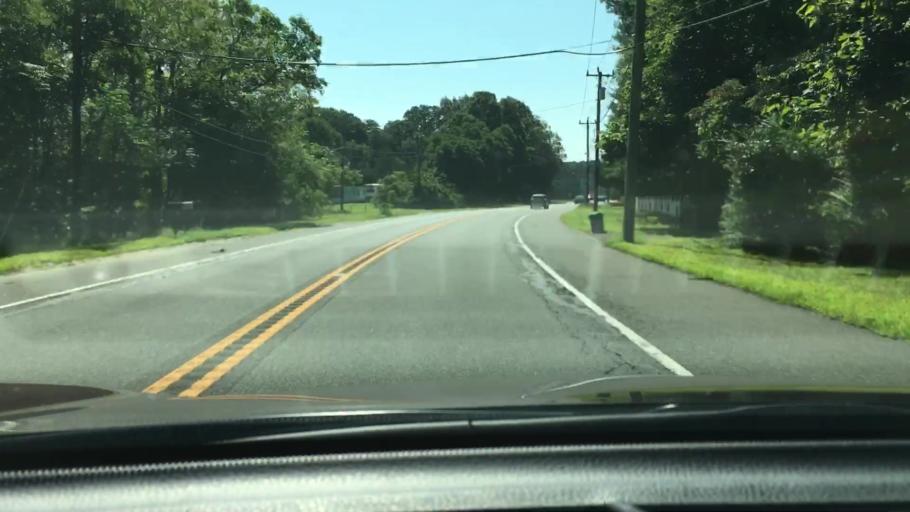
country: US
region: New Jersey
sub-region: Cumberland County
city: Laurel Lake
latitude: 39.3727
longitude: -74.9442
